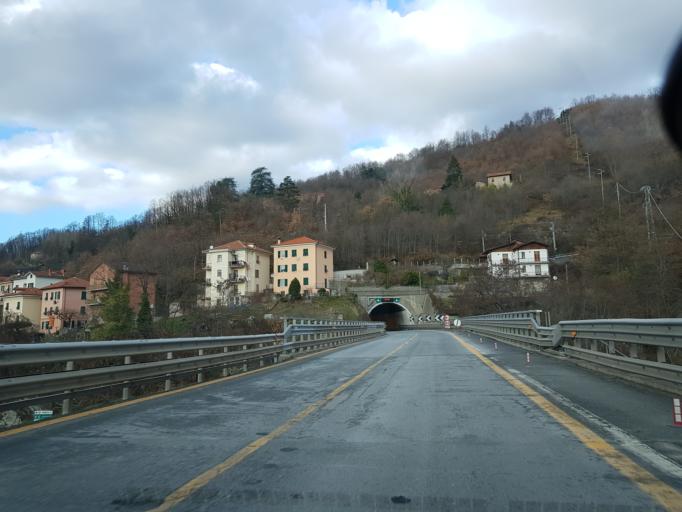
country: IT
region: Liguria
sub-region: Provincia di Genova
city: Ronco Scrivia
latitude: 44.6135
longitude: 8.9565
